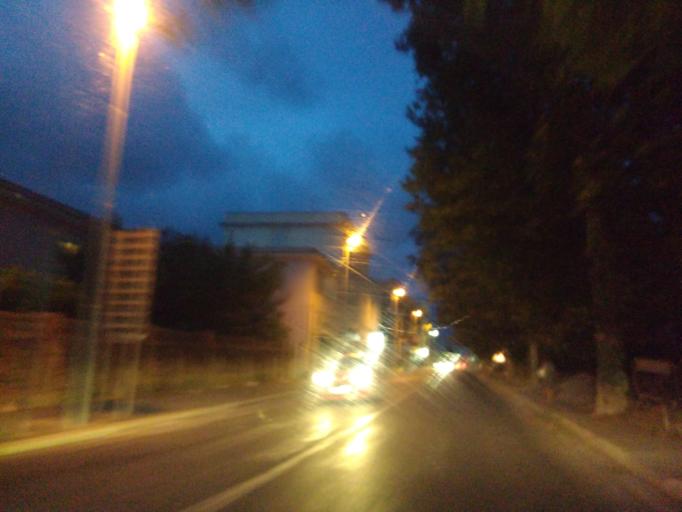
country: IT
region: Latium
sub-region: Citta metropolitana di Roma Capitale
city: Anzio
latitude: 41.4510
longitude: 12.6254
